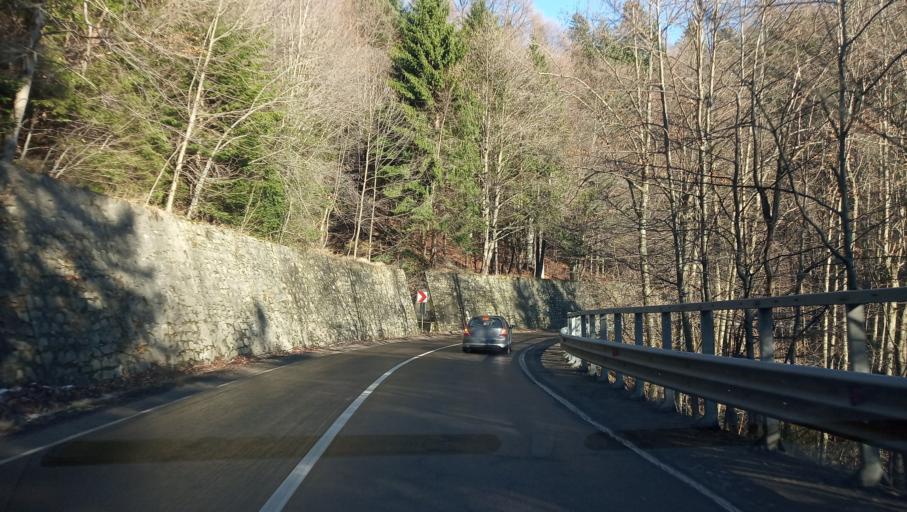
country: RO
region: Brasov
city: Crivina
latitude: 45.4713
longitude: 25.9278
